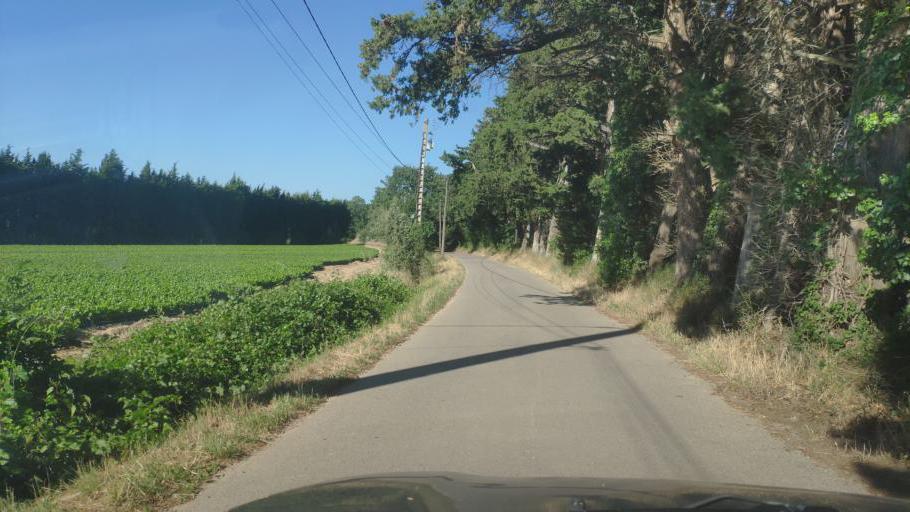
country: FR
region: Provence-Alpes-Cote d'Azur
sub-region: Departement du Vaucluse
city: Loriol-du-Comtat
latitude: 44.0751
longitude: 5.0170
